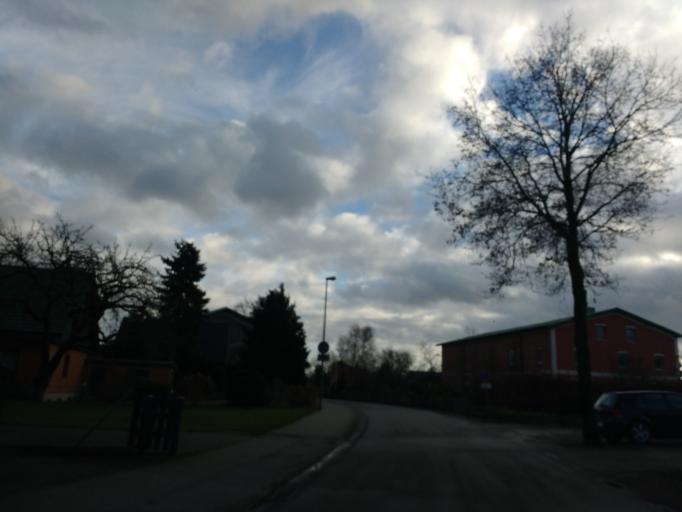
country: DE
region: Schleswig-Holstein
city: Aukrug
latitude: 54.0727
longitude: 9.7967
